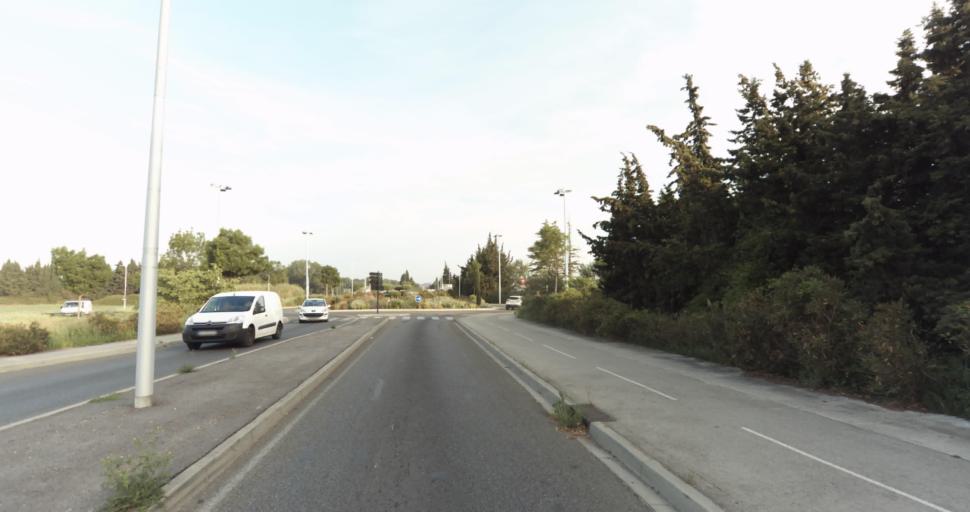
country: FR
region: Languedoc-Roussillon
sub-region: Departement du Gard
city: Caissargues
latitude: 43.8208
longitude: 4.3859
